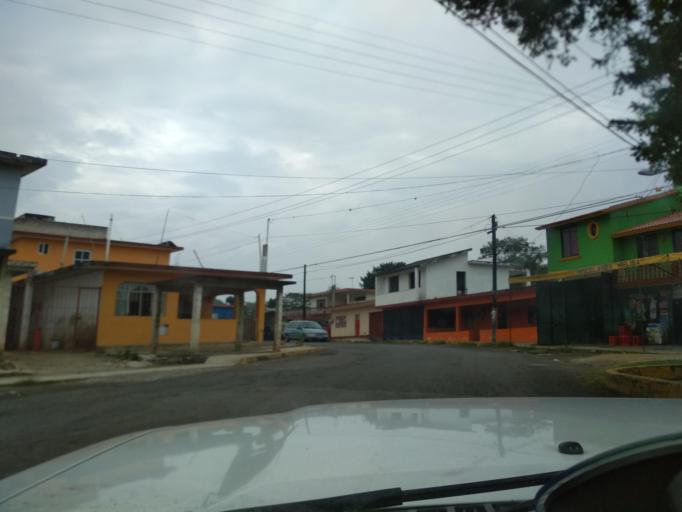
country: MX
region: Veracruz
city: El Castillo
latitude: 19.5637
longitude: -96.8637
